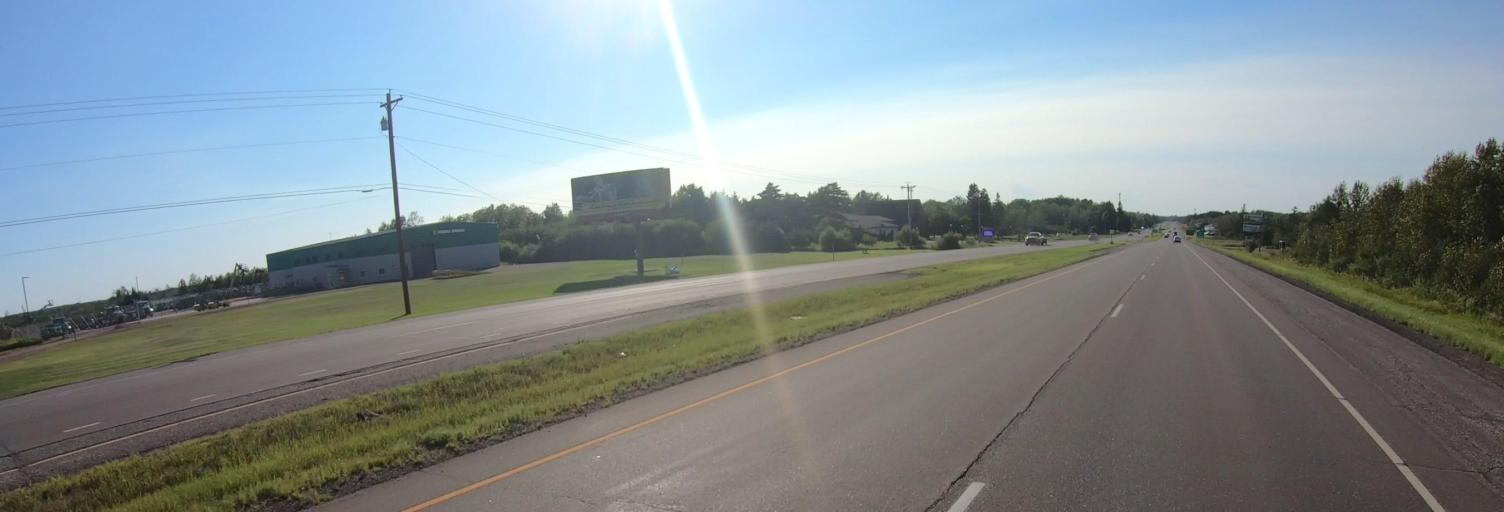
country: US
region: Minnesota
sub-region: Saint Louis County
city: Hermantown
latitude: 46.8405
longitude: -92.2502
